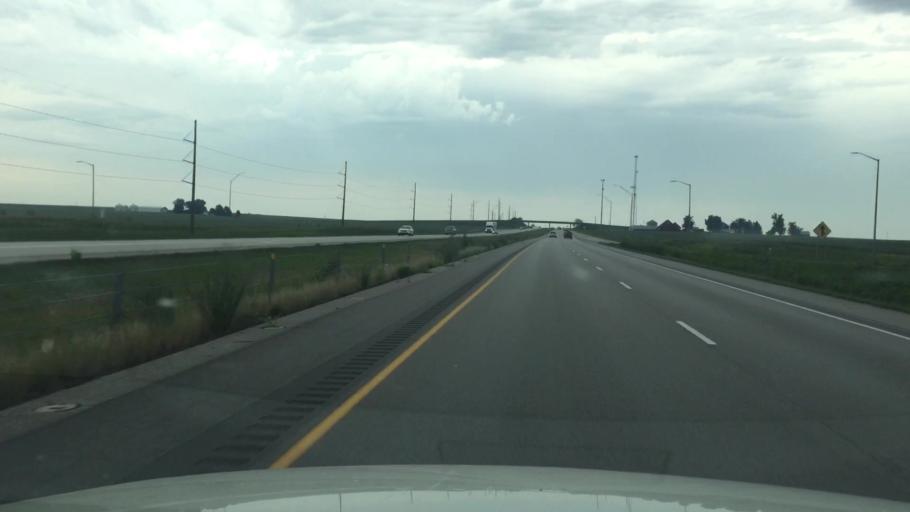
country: US
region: Iowa
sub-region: Story County
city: Huxley
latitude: 41.8284
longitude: -93.5711
